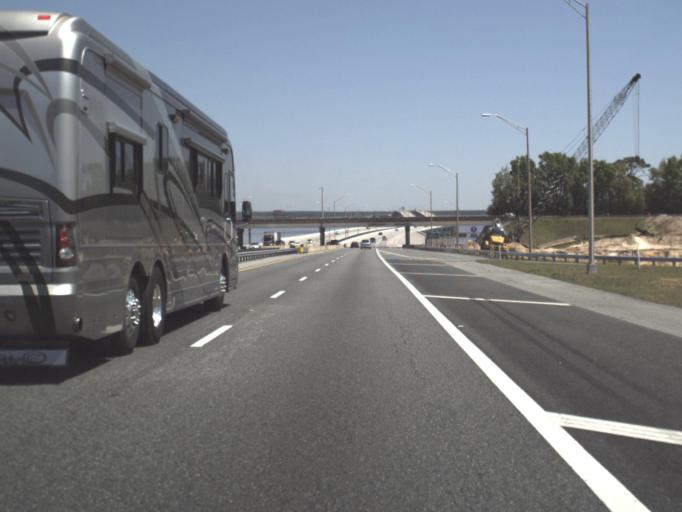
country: US
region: Florida
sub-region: Escambia County
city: Ferry Pass
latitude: 30.5052
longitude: -87.1648
